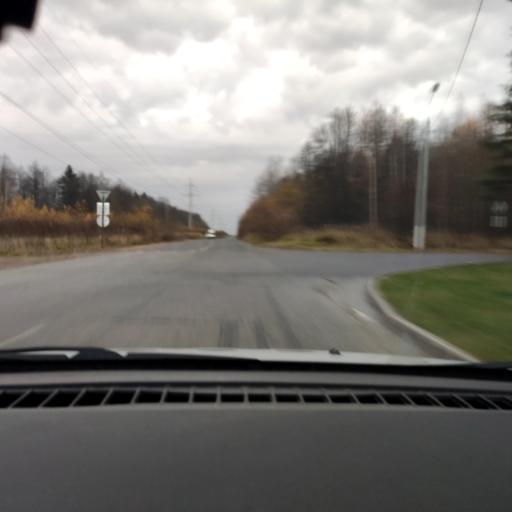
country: RU
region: Perm
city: Perm
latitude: 58.0947
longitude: 56.4028
